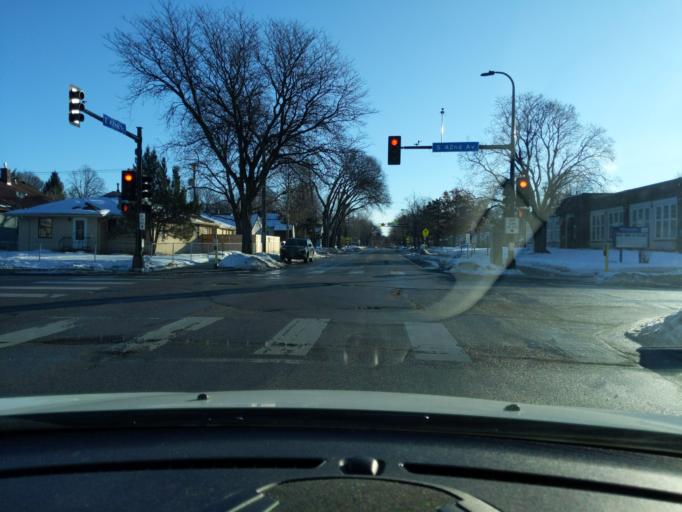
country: US
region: Minnesota
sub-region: Ramsey County
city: Lauderdale
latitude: 44.9270
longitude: -93.2130
